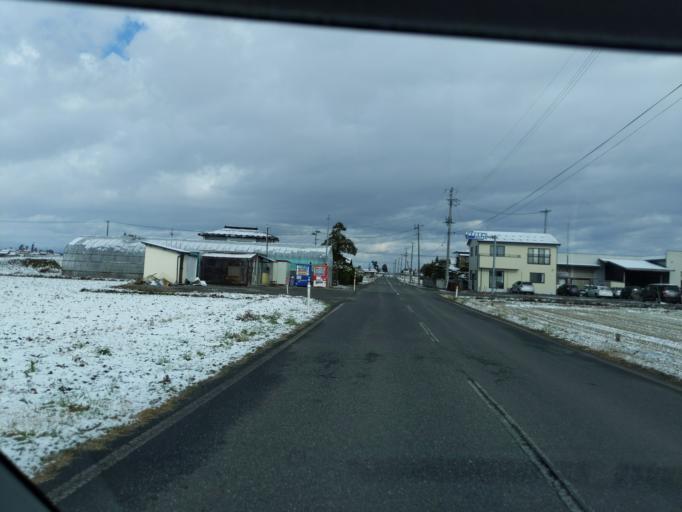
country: JP
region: Iwate
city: Mizusawa
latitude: 39.1504
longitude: 141.1134
